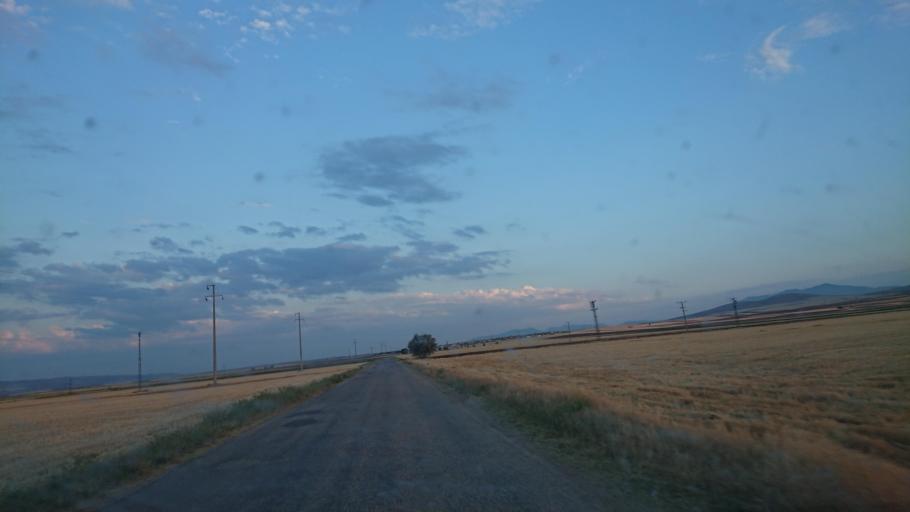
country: TR
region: Aksaray
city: Ortakoy
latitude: 38.8525
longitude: 34.0773
